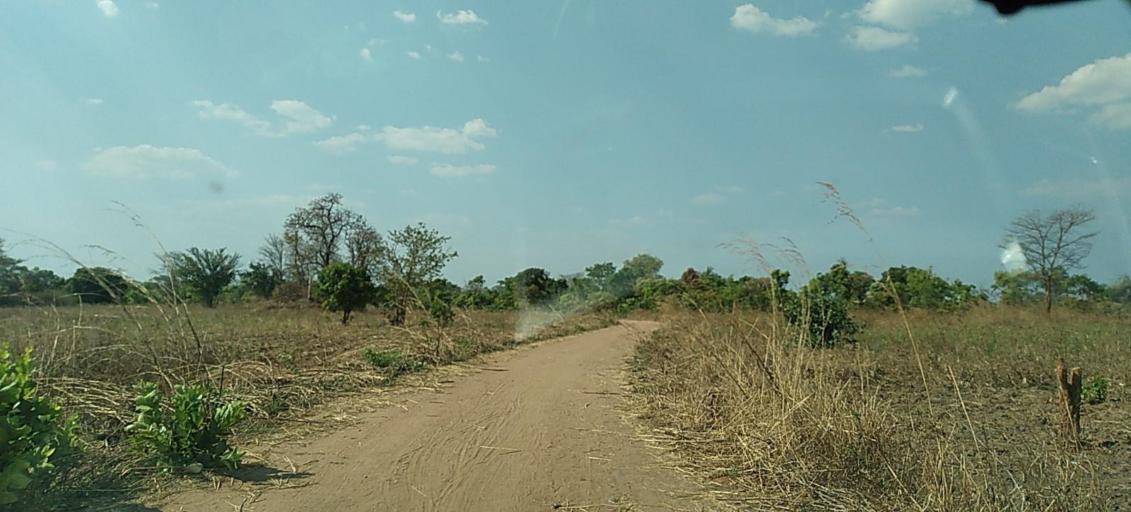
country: ZM
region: North-Western
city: Kalengwa
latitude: -13.1096
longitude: 24.9925
